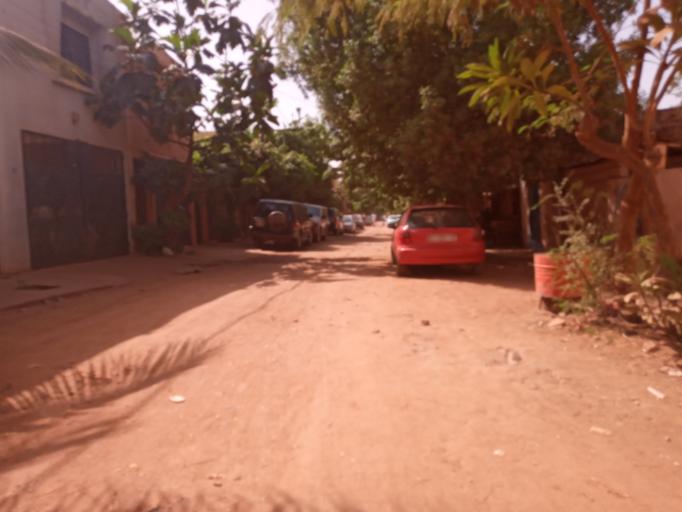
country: ML
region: Bamako
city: Bamako
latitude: 12.5857
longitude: -7.9498
